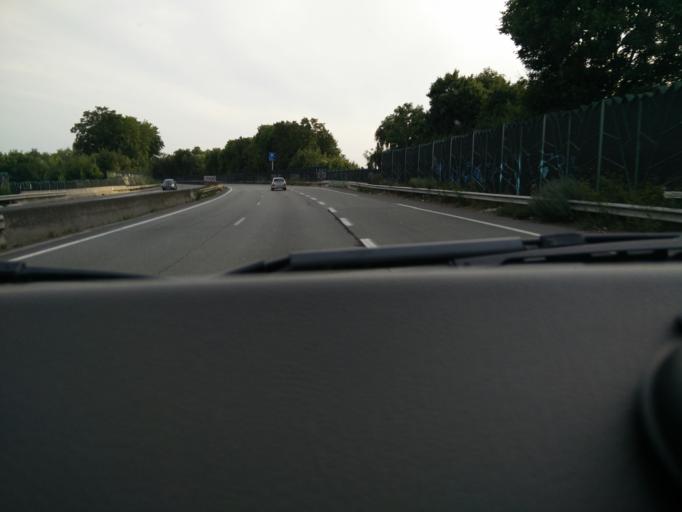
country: FR
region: Nord-Pas-de-Calais
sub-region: Departement du Nord
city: La Sentinelle
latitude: 50.3532
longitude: 3.4801
